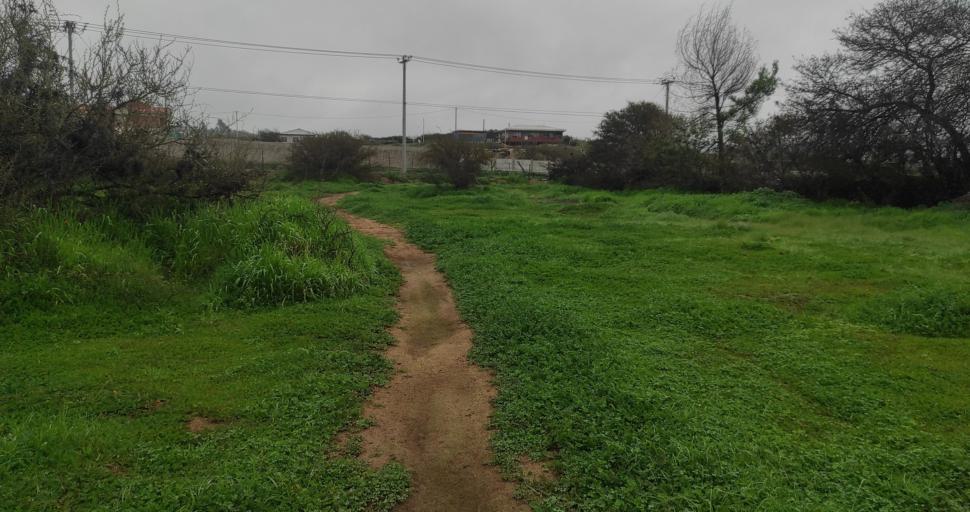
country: CL
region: Valparaiso
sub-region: Provincia de Marga Marga
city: Limache
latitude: -33.0218
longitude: -71.2604
